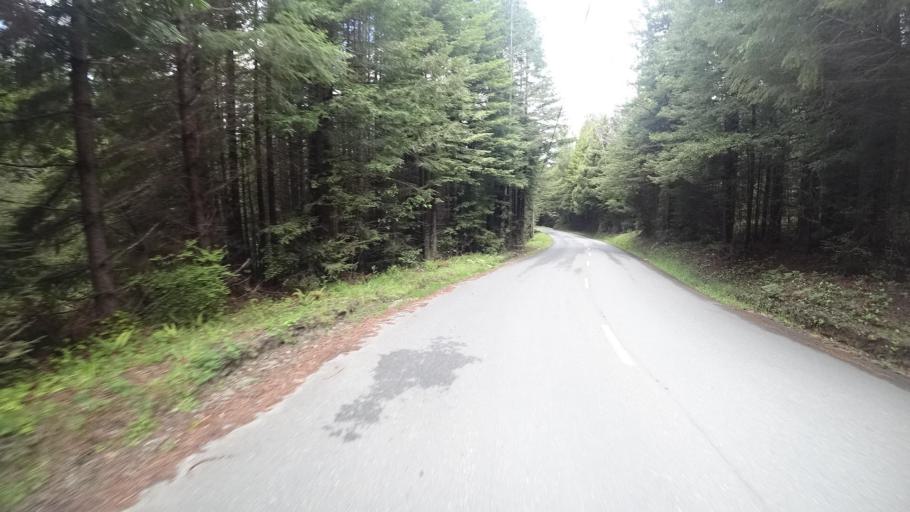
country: US
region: California
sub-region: Humboldt County
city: Blue Lake
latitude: 40.8679
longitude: -123.9537
